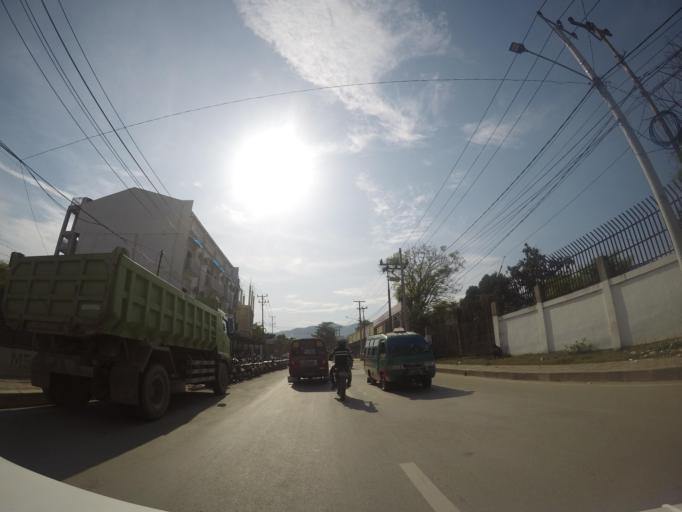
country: TL
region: Dili
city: Dili
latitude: -8.5599
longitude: 125.5962
